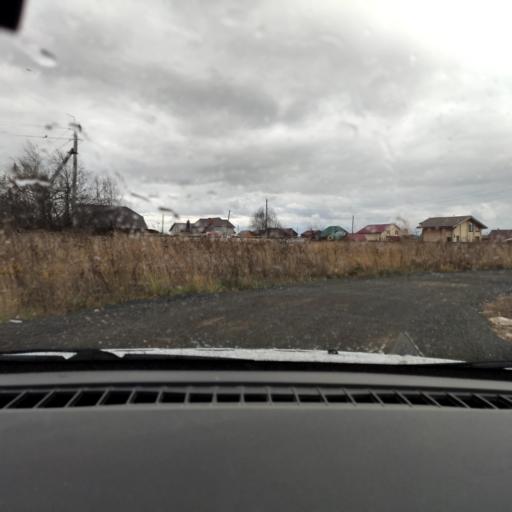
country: RU
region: Perm
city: Kultayevo
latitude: 57.8982
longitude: 55.9557
